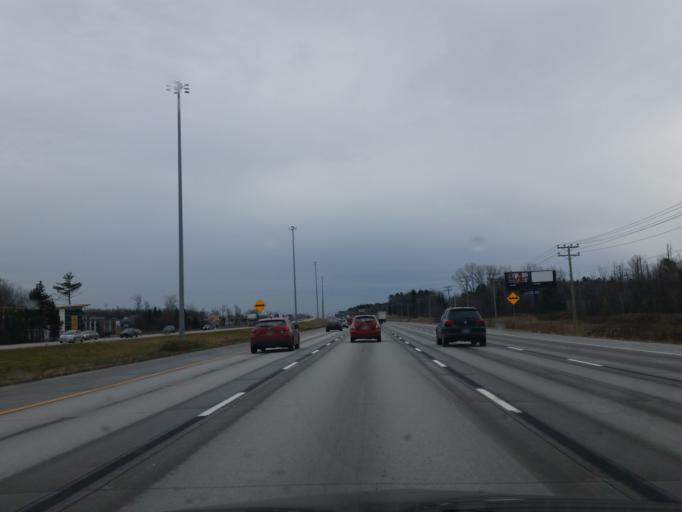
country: CA
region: Quebec
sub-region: Laurentides
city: Blainville
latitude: 45.6745
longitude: -73.9108
